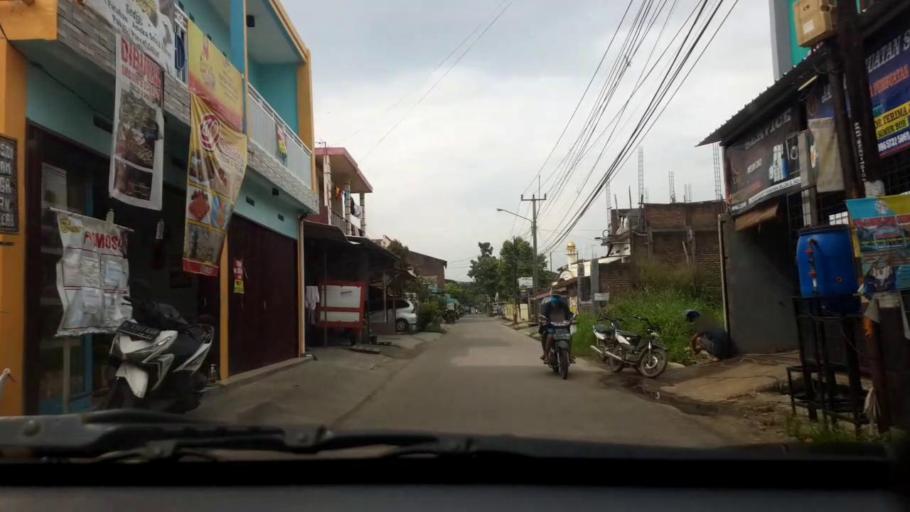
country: ID
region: West Java
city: Cileunyi
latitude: -6.9451
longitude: 107.7213
